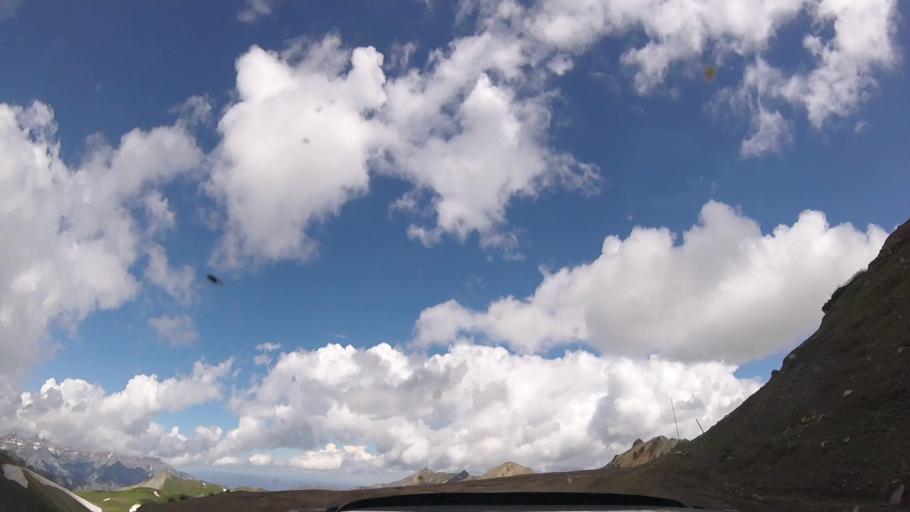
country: US
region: Colorado
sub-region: Ouray County
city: Ouray
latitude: 37.9697
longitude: -107.5902
